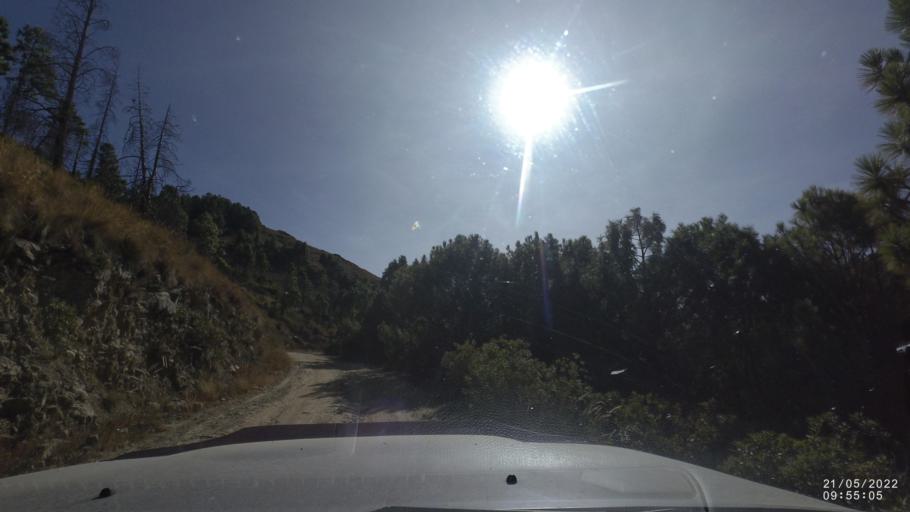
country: BO
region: Cochabamba
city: Colomi
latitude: -17.3412
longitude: -65.9904
